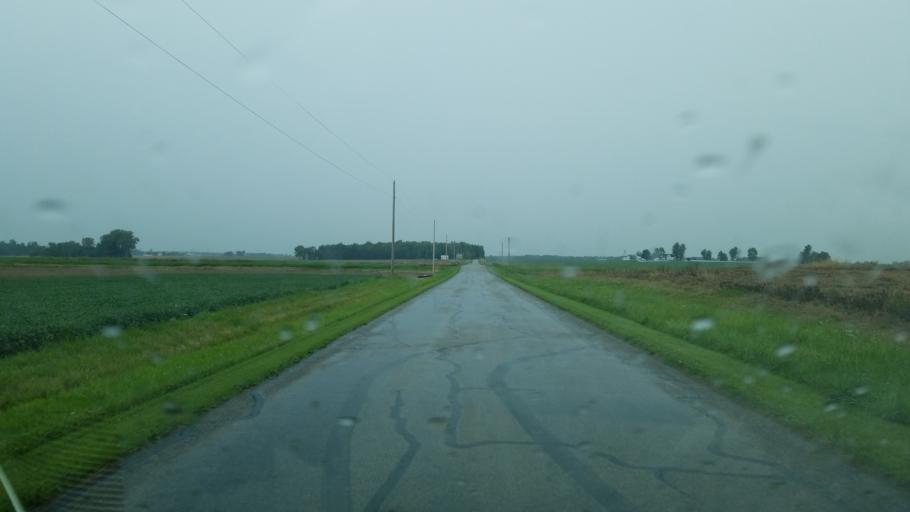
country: US
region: Ohio
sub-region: Huron County
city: Willard
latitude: 41.0250
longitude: -82.8126
